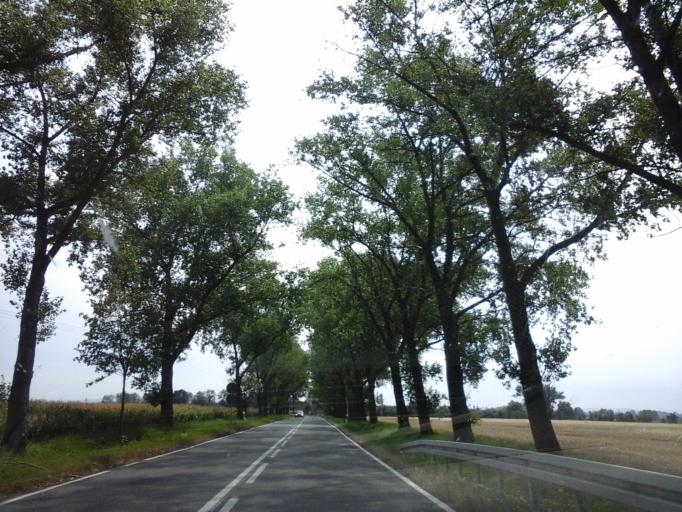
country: PL
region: Lower Silesian Voivodeship
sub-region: Powiat strzelinski
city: Strzelin
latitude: 50.8543
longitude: 17.0601
